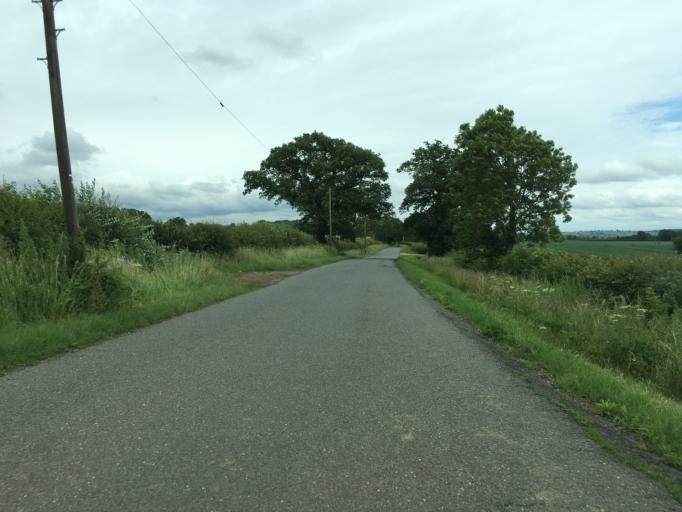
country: GB
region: England
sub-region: Northamptonshire
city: Daventry
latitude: 52.2416
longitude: -1.1881
